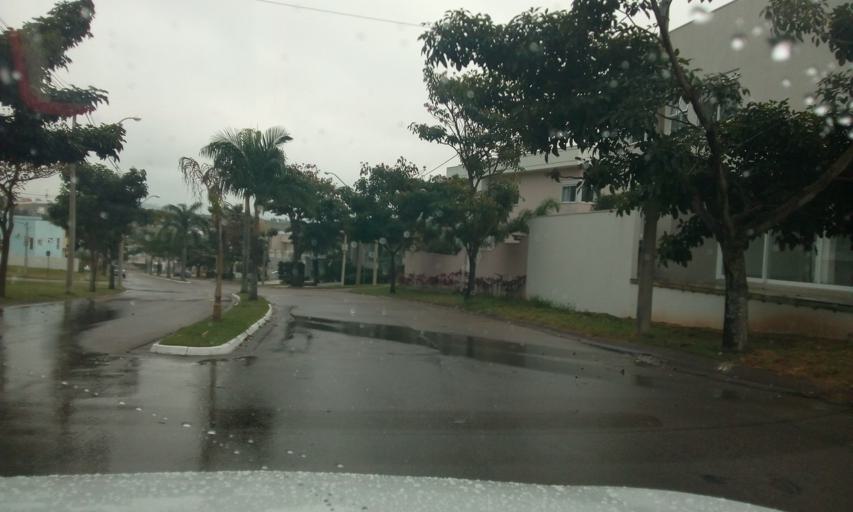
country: BR
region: Sao Paulo
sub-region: Itupeva
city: Itupeva
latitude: -23.1408
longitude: -47.0527
